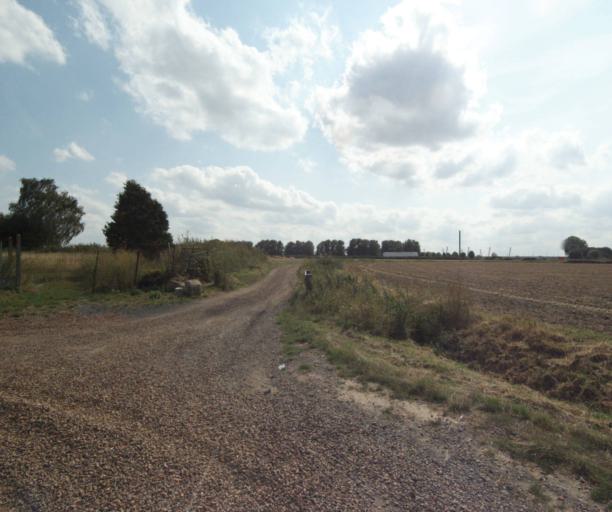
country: FR
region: Nord-Pas-de-Calais
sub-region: Departement du Nord
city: Lannoy
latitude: 50.6589
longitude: 3.2086
